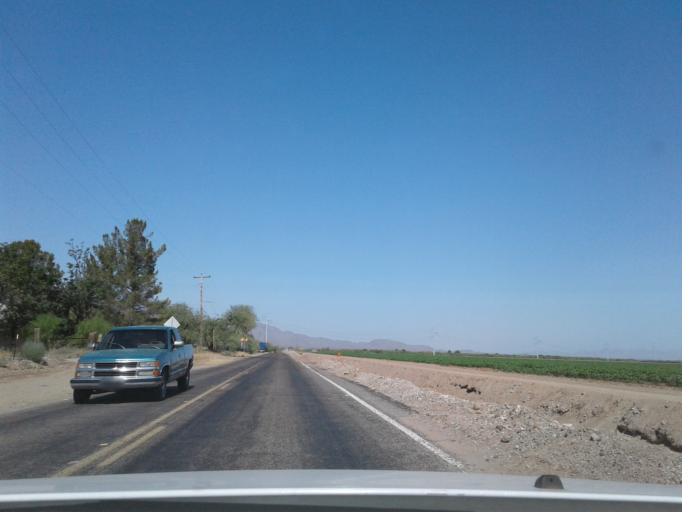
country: US
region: Arizona
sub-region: Maricopa County
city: Laveen
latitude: 33.3339
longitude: -112.1703
